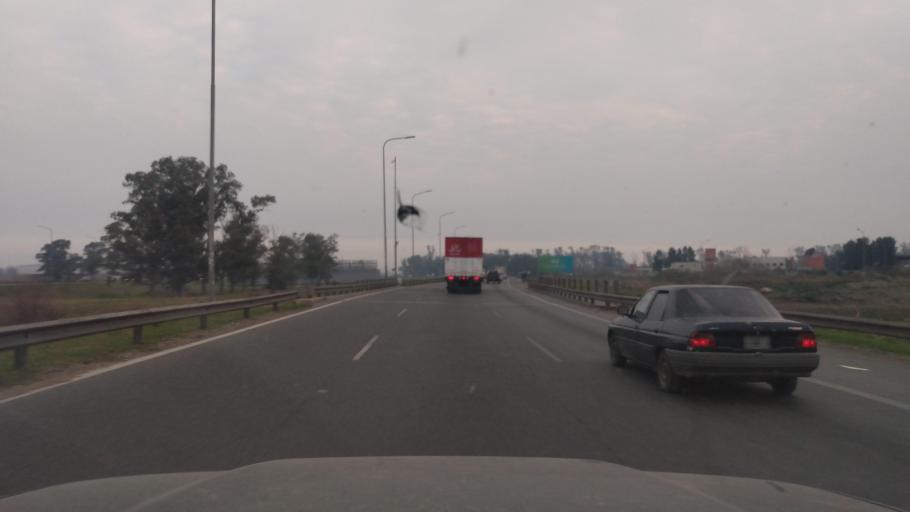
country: AR
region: Buenos Aires
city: Hurlingham
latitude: -34.5215
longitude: -58.5917
